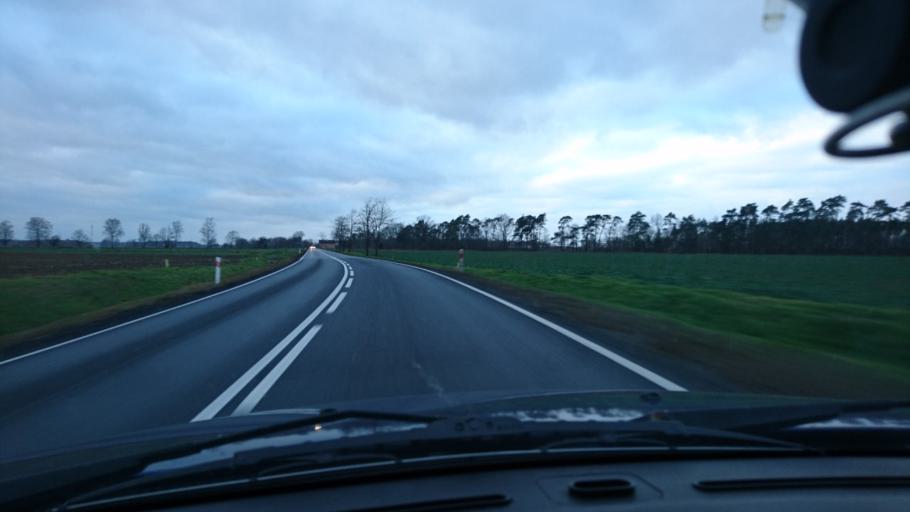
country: PL
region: Opole Voivodeship
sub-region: Powiat kluczborski
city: Byczyna
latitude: 51.1507
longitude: 18.1842
